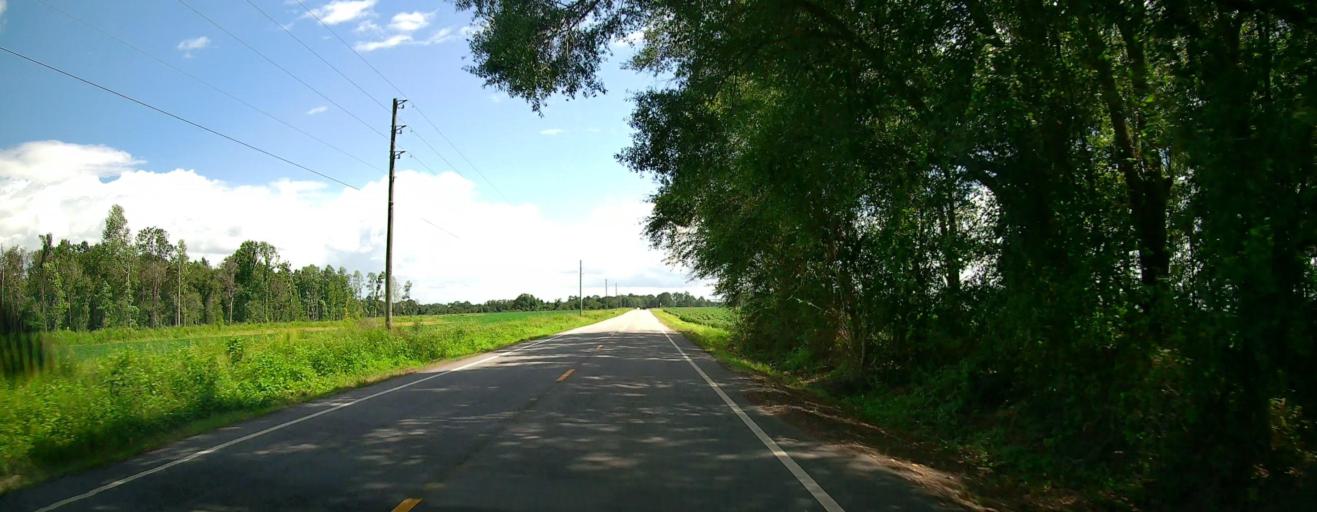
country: US
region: Georgia
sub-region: Irwin County
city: Ocilla
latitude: 31.6516
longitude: -83.1739
